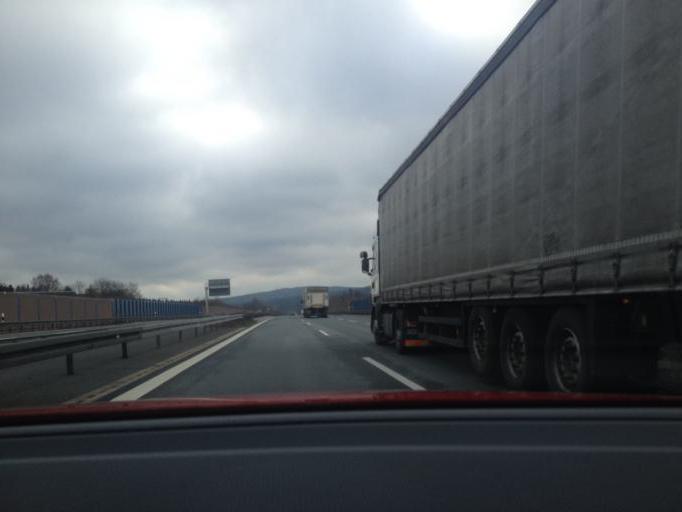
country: DE
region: Bavaria
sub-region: Upper Franconia
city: Rehau
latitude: 50.2452
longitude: 12.0609
